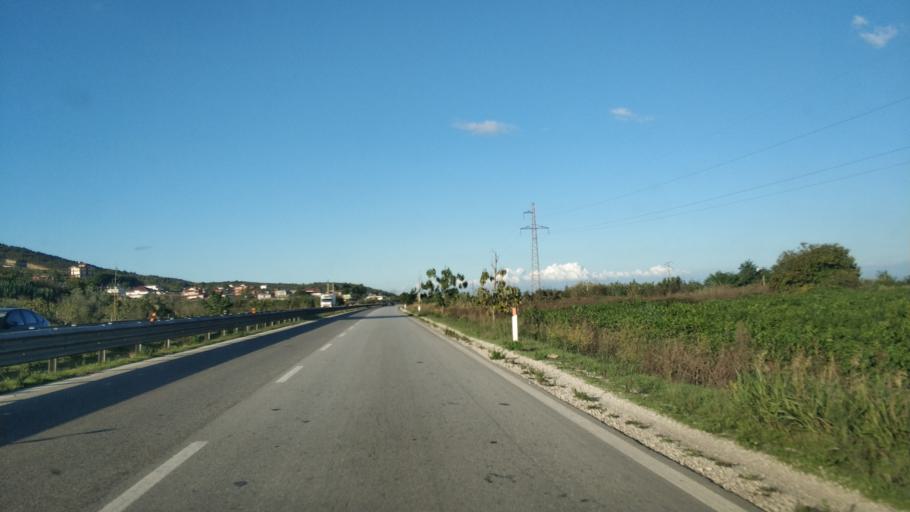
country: AL
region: Fier
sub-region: Rrethi i Lushnjes
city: Kolonje
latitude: 40.7881
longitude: 19.5991
